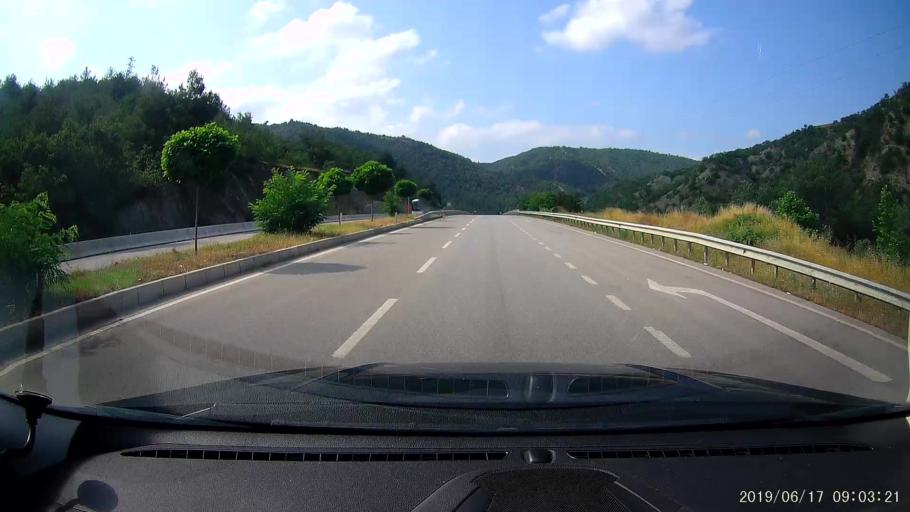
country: TR
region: Amasya
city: Tasova
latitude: 40.7567
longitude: 36.3023
